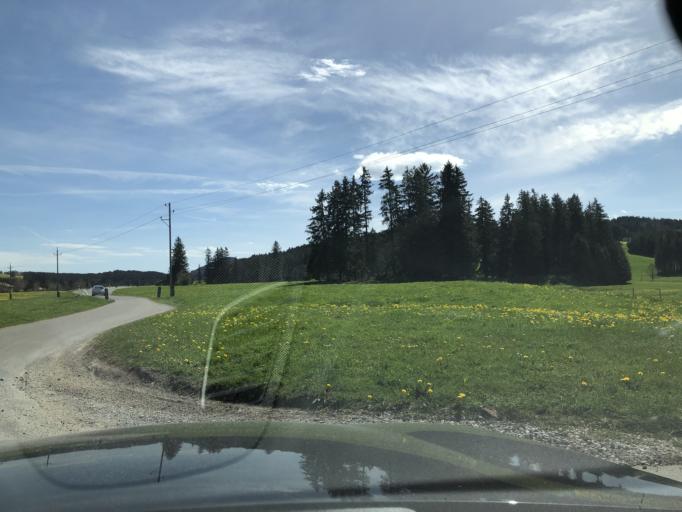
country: DE
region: Bavaria
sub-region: Swabia
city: Seeg
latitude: 47.6400
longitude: 10.6067
